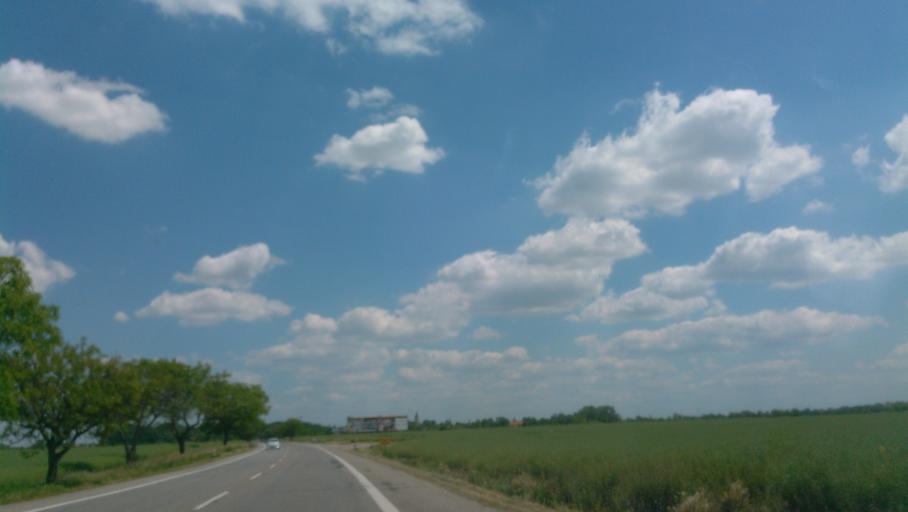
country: SK
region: Trnavsky
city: Samorin
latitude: 48.0104
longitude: 17.3537
